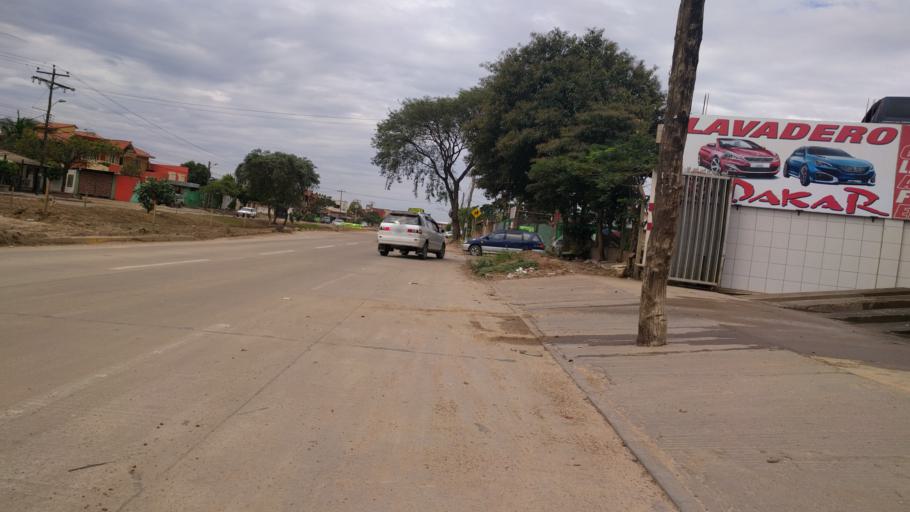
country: BO
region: Santa Cruz
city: Santa Cruz de la Sierra
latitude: -17.8364
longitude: -63.1746
